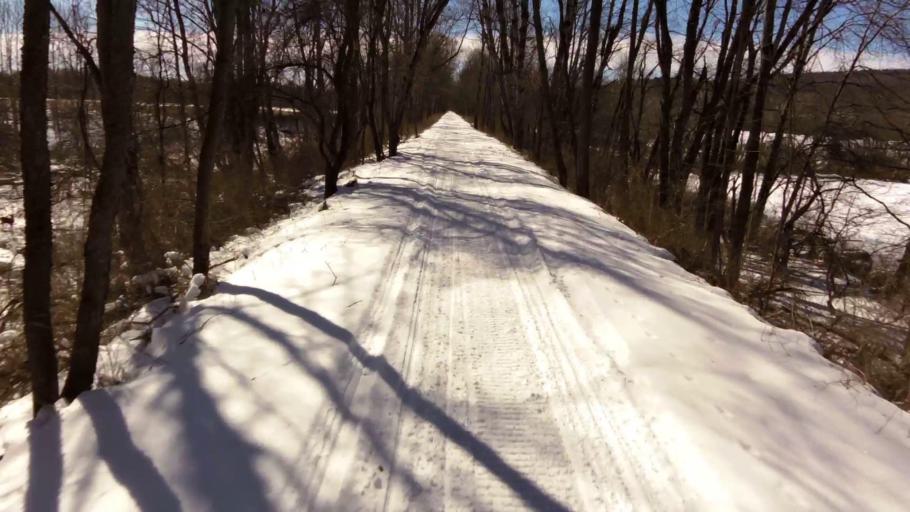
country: US
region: New York
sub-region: Allegany County
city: Houghton
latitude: 42.3511
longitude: -78.1253
